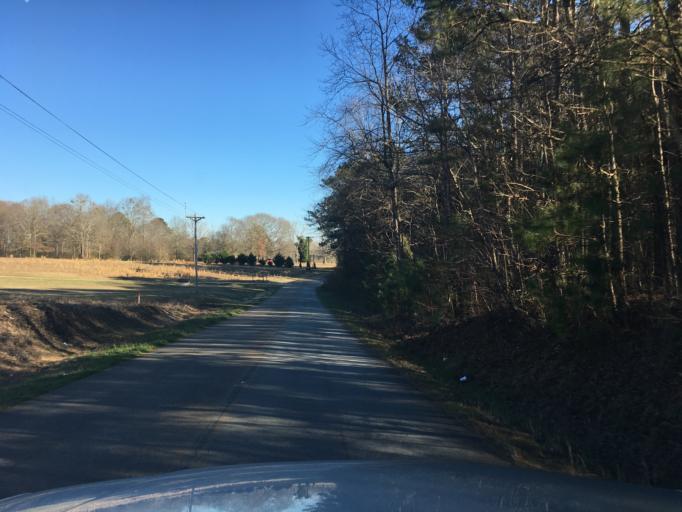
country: US
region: Georgia
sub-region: Carroll County
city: Carrollton
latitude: 33.4400
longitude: -85.1203
